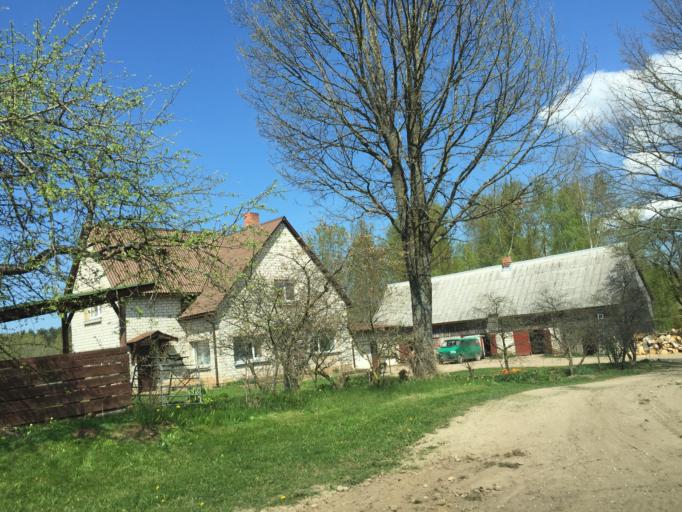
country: LV
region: Saulkrastu
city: Saulkrasti
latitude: 57.3380
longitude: 24.4799
